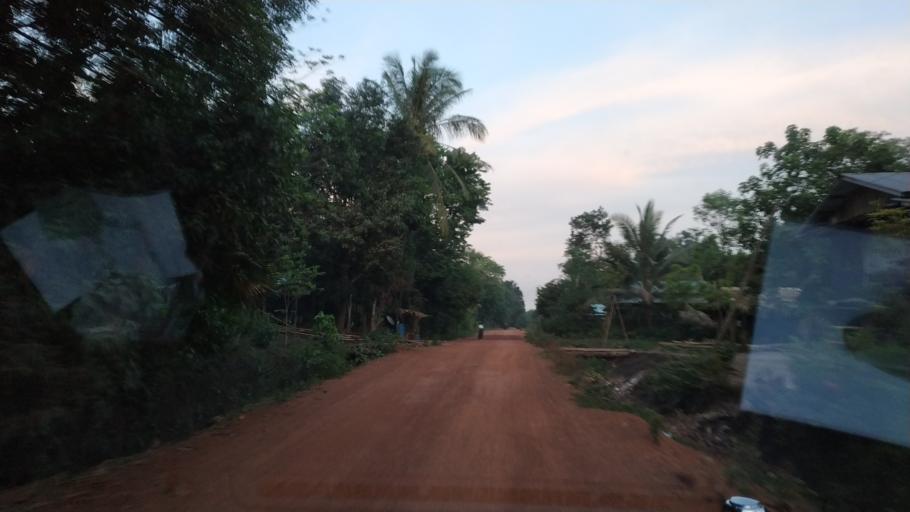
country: MM
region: Mon
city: Kyaikto
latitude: 17.4238
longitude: 97.0471
